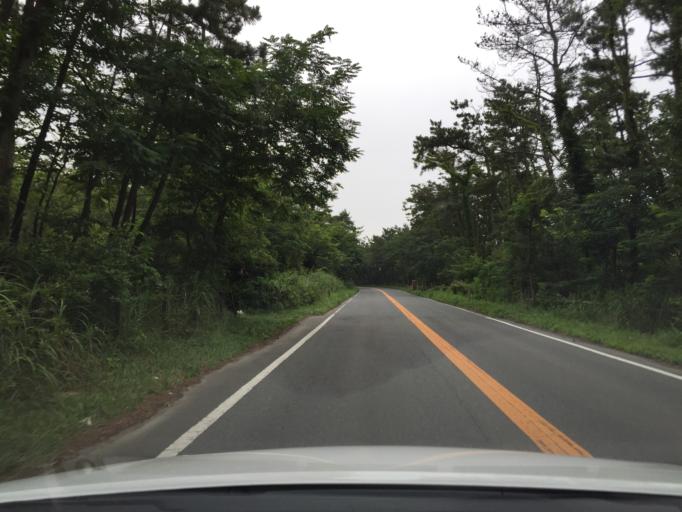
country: JP
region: Fukushima
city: Iwaki
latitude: 37.0252
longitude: 140.9712
